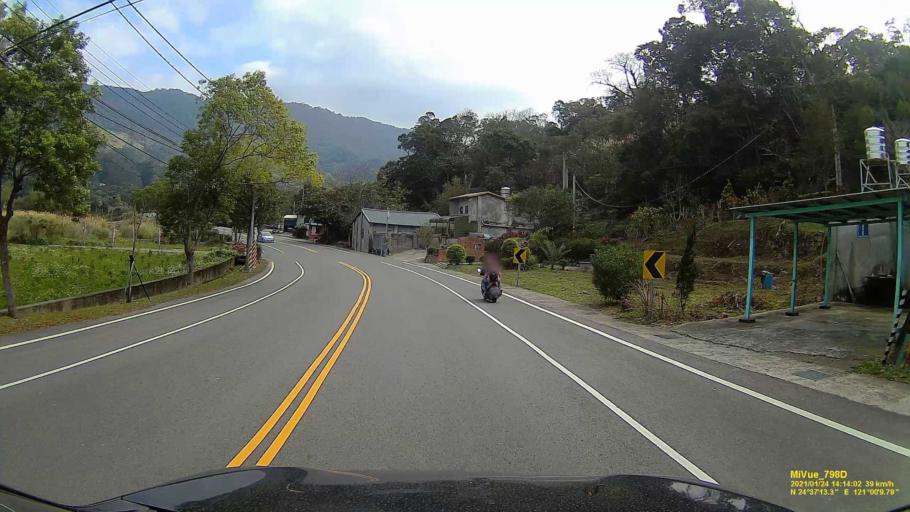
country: TW
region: Taiwan
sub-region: Hsinchu
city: Hsinchu
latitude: 24.6201
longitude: 121.0029
